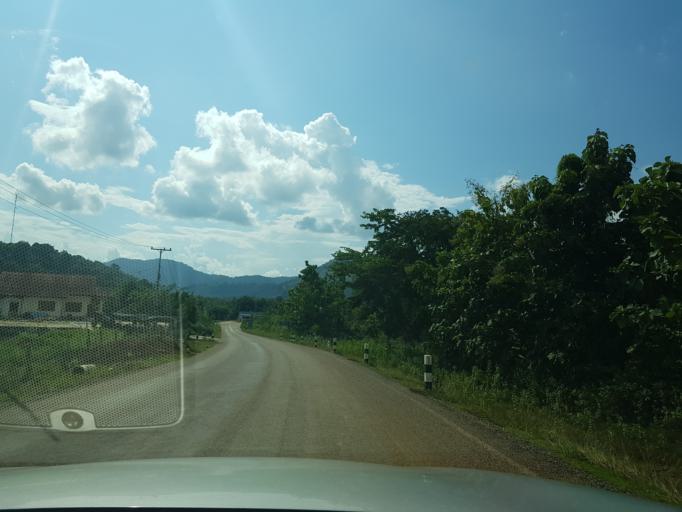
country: TH
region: Nong Khai
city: Sangkhom
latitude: 18.1855
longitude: 102.1851
